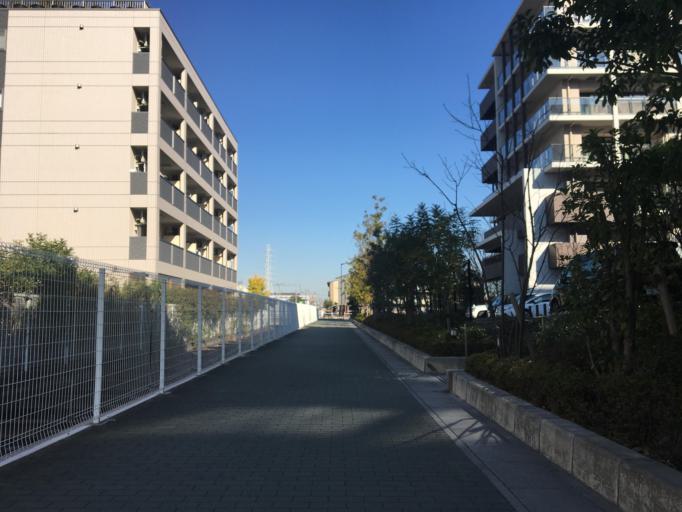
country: JP
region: Saitama
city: Yashio-shi
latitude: 35.8075
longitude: 139.8497
